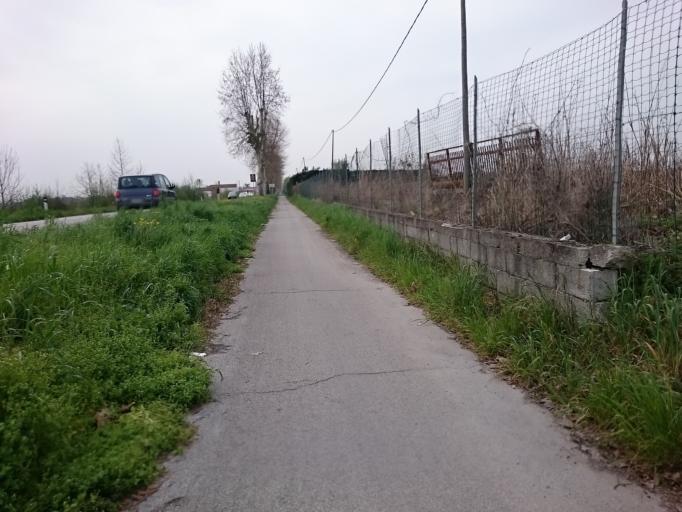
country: IT
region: Veneto
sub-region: Provincia di Padova
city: Bagnoli di Sopra
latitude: 45.1959
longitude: 11.8861
